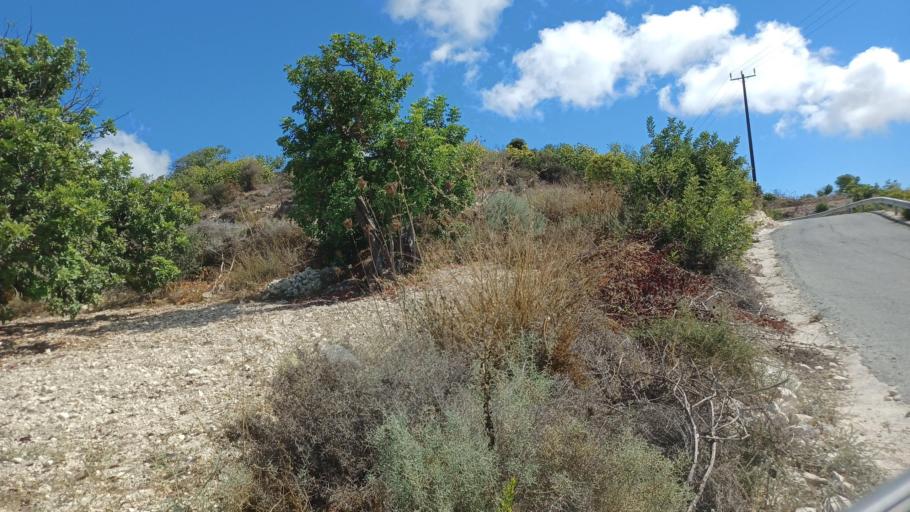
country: CY
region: Pafos
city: Tala
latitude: 34.8566
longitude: 32.4379
